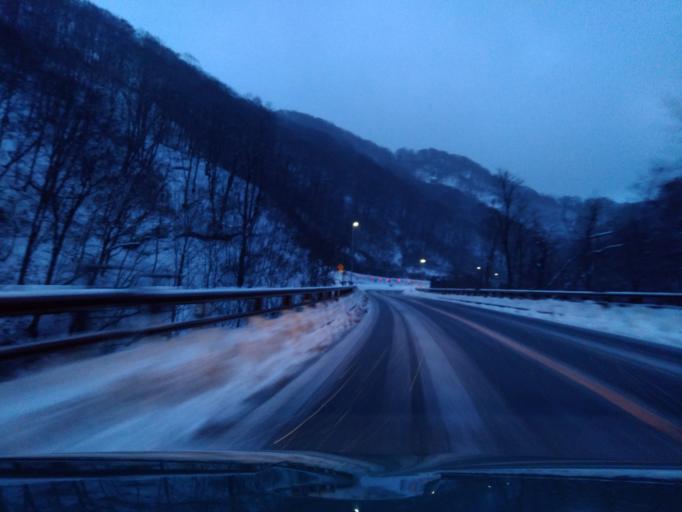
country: JP
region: Iwate
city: Shizukuishi
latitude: 39.7196
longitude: 140.8214
